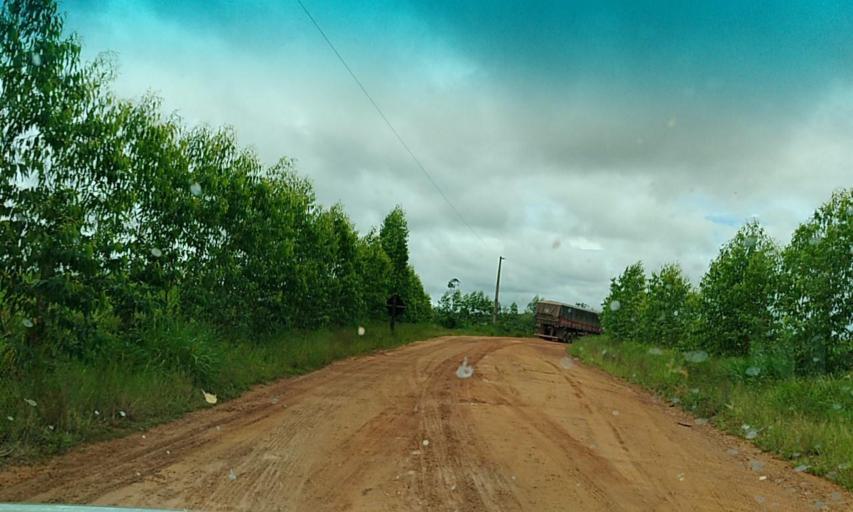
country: BR
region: Para
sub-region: Altamira
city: Altamira
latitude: -3.0608
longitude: -51.7225
